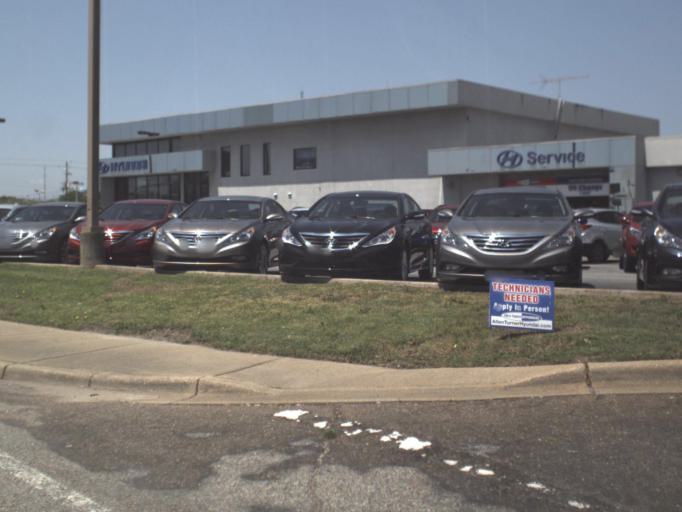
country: US
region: Florida
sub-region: Escambia County
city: Brent
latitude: 30.4748
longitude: -87.2474
